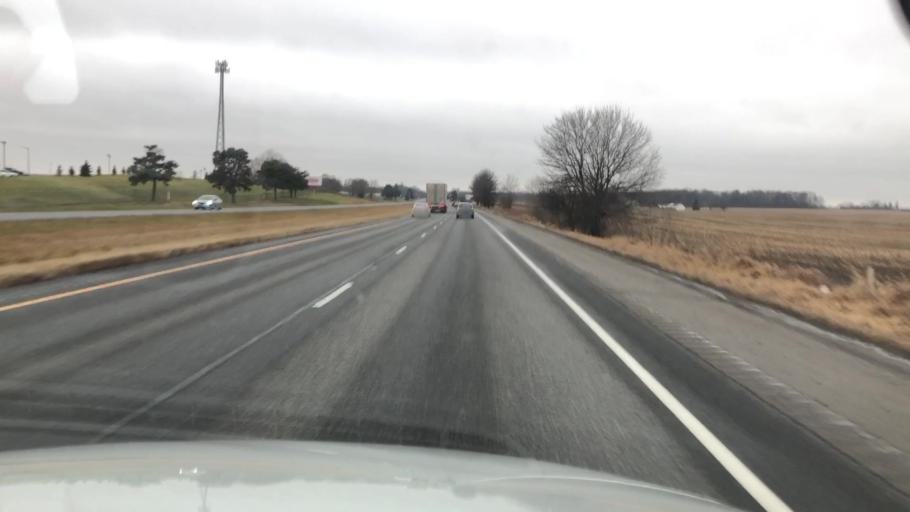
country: US
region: Indiana
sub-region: Whitley County
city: Churubusco
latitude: 41.1267
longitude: -85.3473
